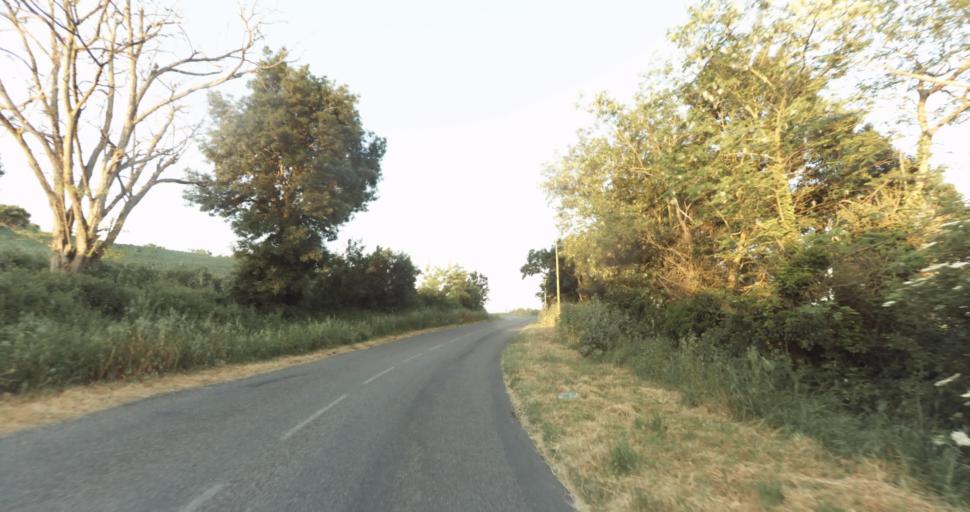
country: FR
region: Midi-Pyrenees
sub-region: Departement du Gers
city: Pujaudran
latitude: 43.6125
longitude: 1.1584
